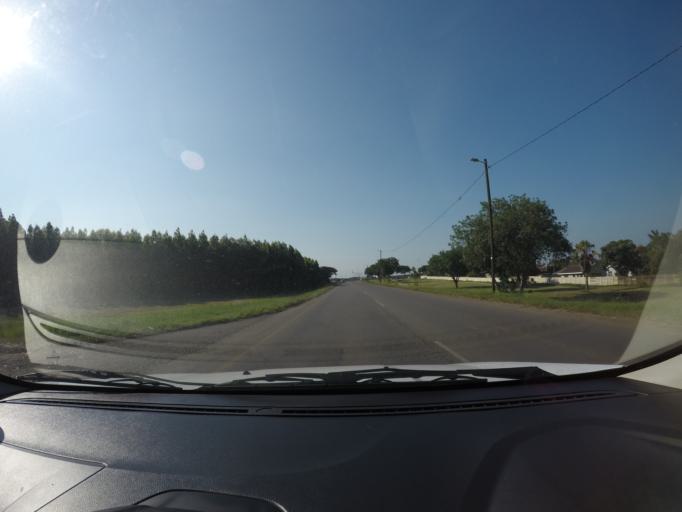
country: ZA
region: KwaZulu-Natal
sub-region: uThungulu District Municipality
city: Richards Bay
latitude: -28.7171
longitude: 32.0316
